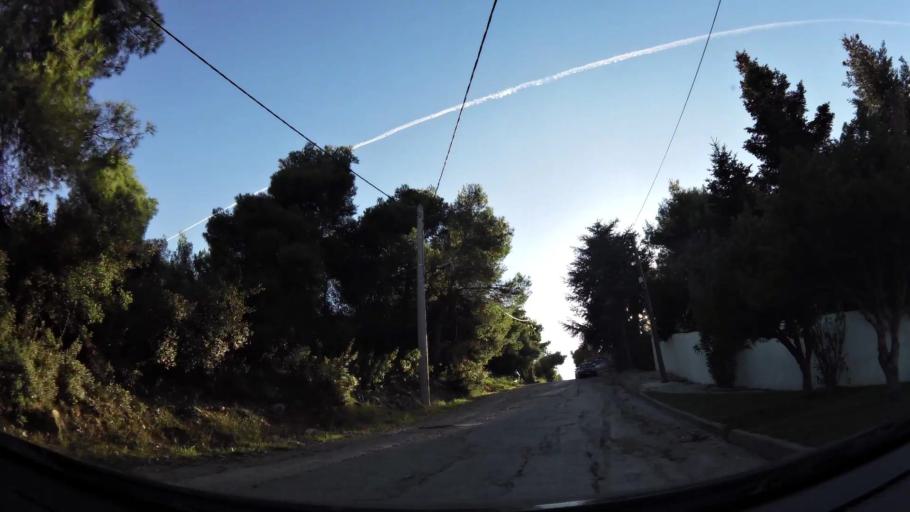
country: GR
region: Attica
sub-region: Nomarchia Anatolikis Attikis
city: Drosia
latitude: 38.1090
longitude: 23.8528
